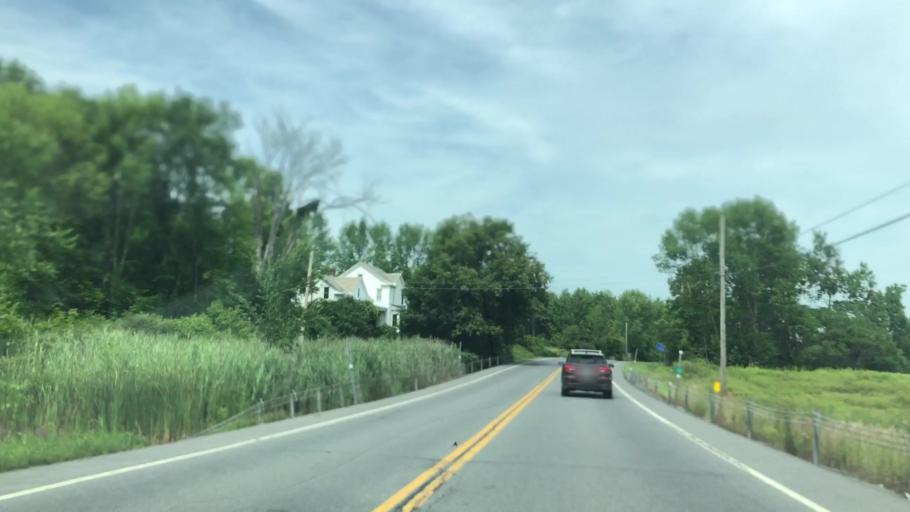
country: US
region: New York
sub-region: Washington County
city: Whitehall
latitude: 43.5010
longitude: -73.4242
